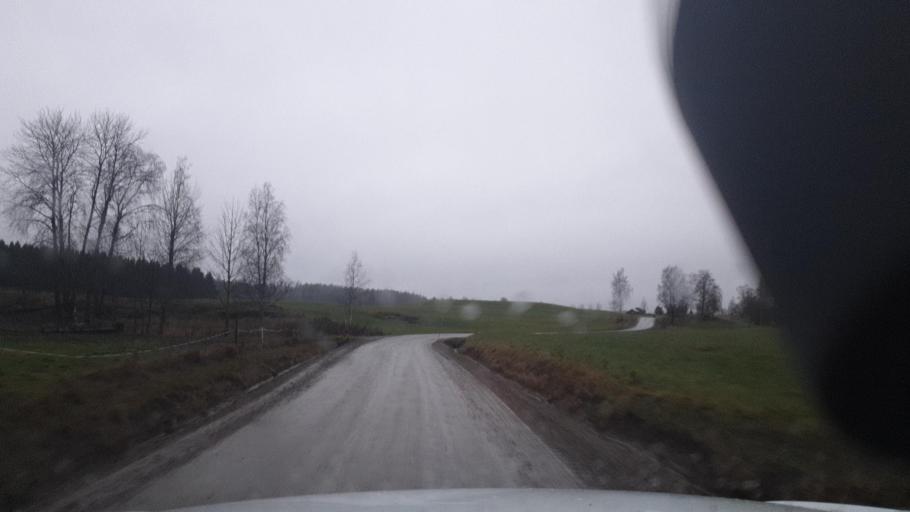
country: SE
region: Vaermland
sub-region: Eda Kommun
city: Amotfors
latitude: 59.7196
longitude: 12.1443
